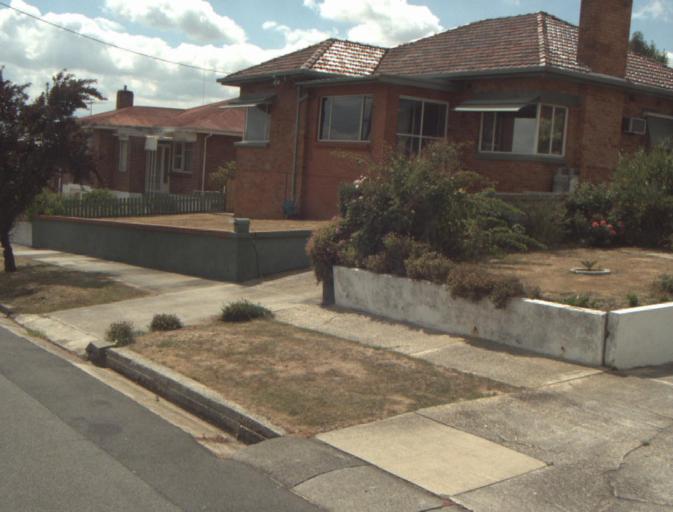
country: AU
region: Tasmania
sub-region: Launceston
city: Summerhill
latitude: -41.4679
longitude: 147.1517
